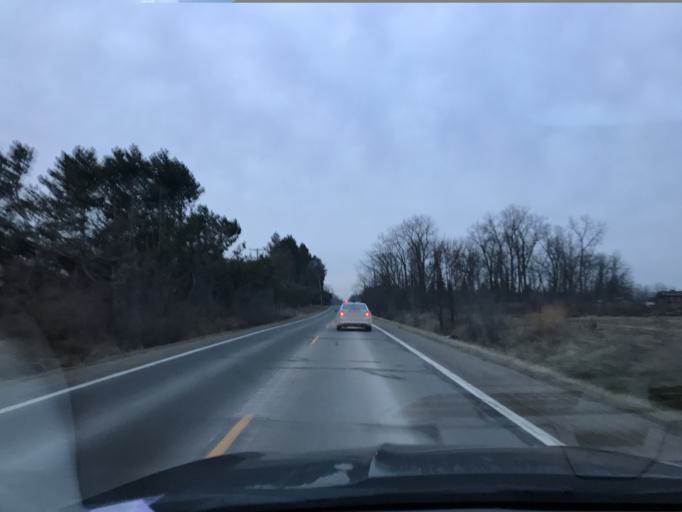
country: US
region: Michigan
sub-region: Macomb County
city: Romeo
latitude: 42.8122
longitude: -82.9628
